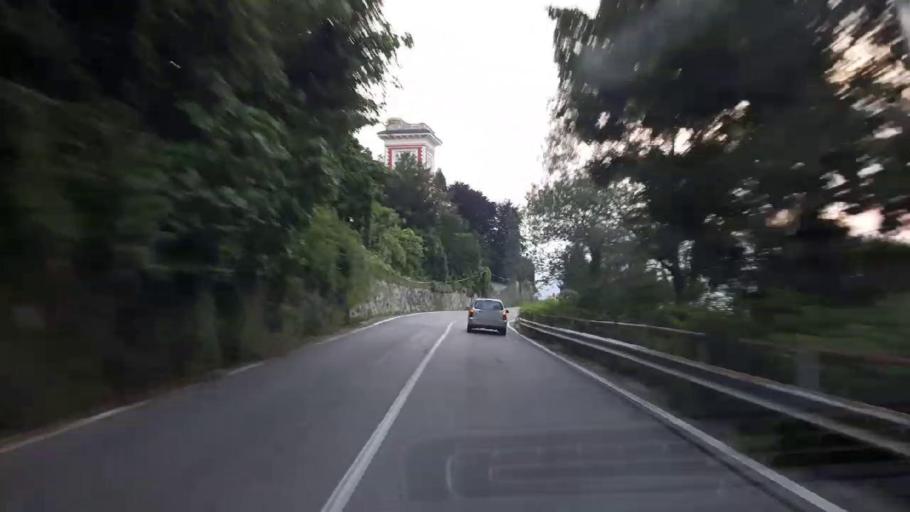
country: IT
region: Piedmont
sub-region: Provincia Verbano-Cusio-Ossola
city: Stresa
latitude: 45.8793
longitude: 8.5550
